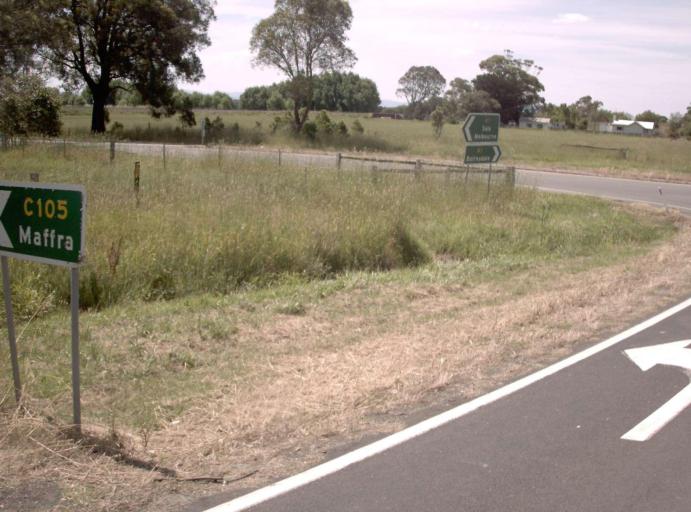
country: AU
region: Victoria
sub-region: Wellington
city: Sale
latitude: -37.9823
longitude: 147.0717
